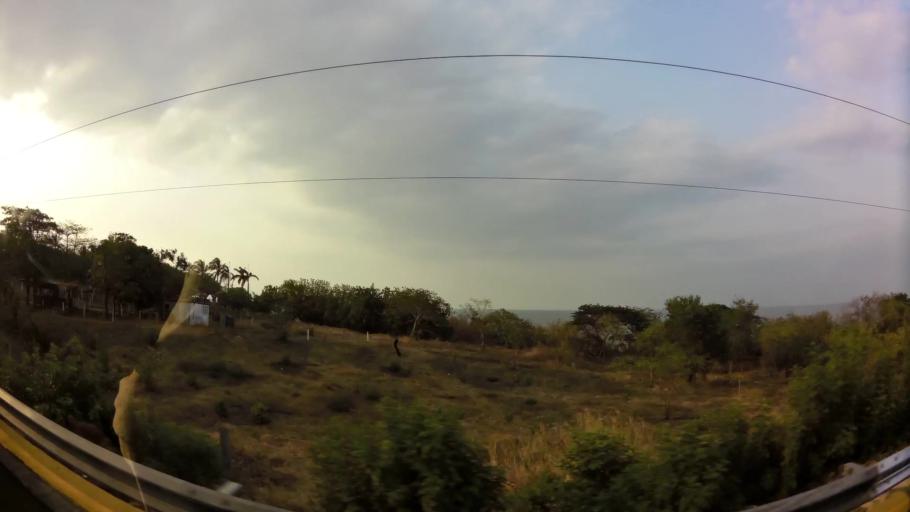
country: NI
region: Leon
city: Nagarote
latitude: 12.2679
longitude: -86.4756
